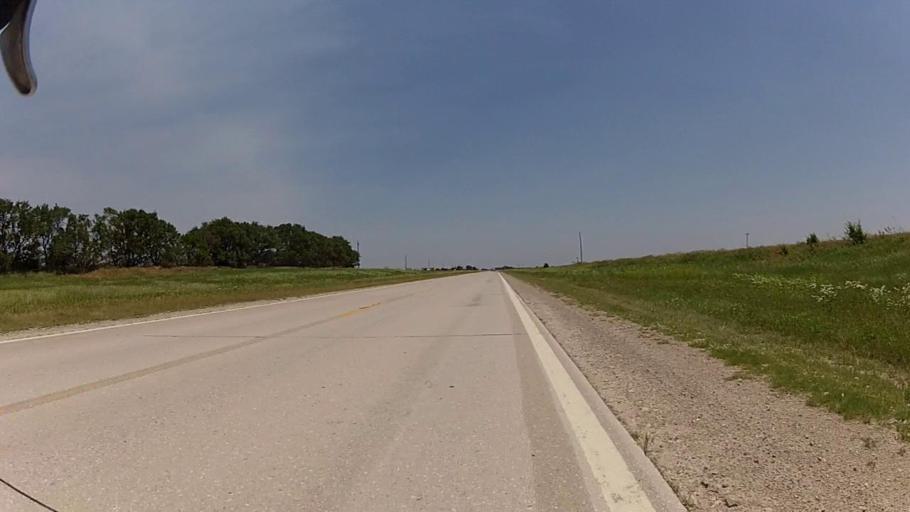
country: US
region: Kansas
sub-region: Sumner County
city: Wellington
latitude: 37.0566
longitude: -97.3847
